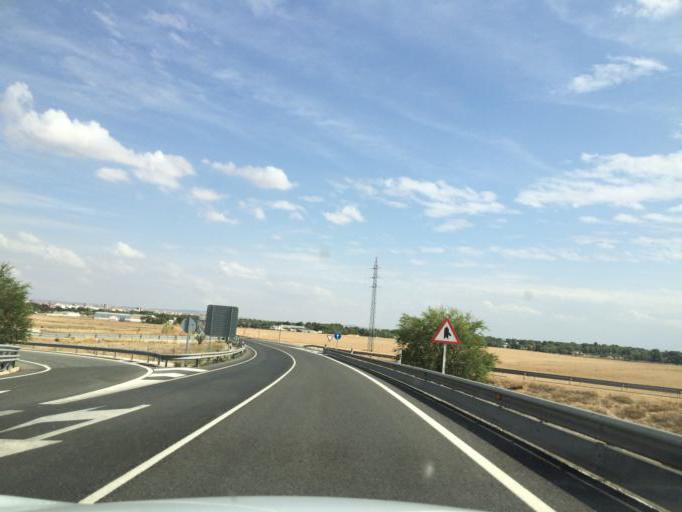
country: ES
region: Castille-La Mancha
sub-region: Provincia de Albacete
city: Albacete
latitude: 39.0014
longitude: -1.9024
